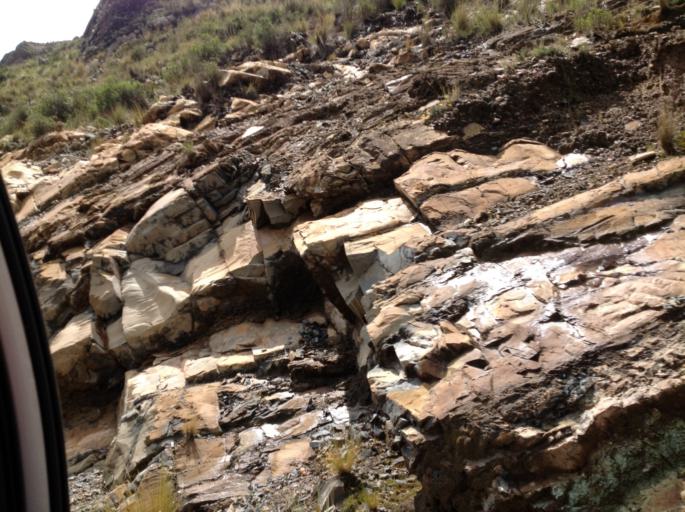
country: BO
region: La Paz
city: Yumani
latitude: -15.7743
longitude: -69.0056
